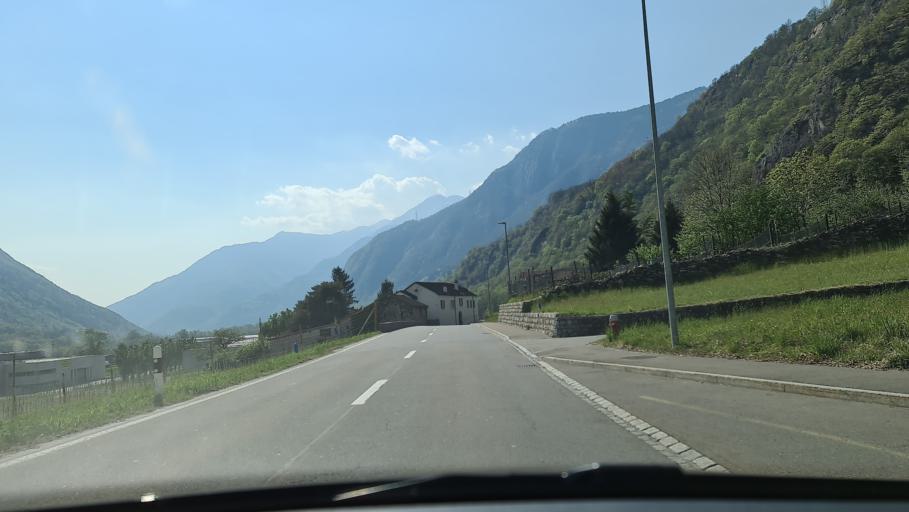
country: CH
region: Grisons
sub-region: Moesa District
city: Roveredo
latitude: 46.2377
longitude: 9.1006
